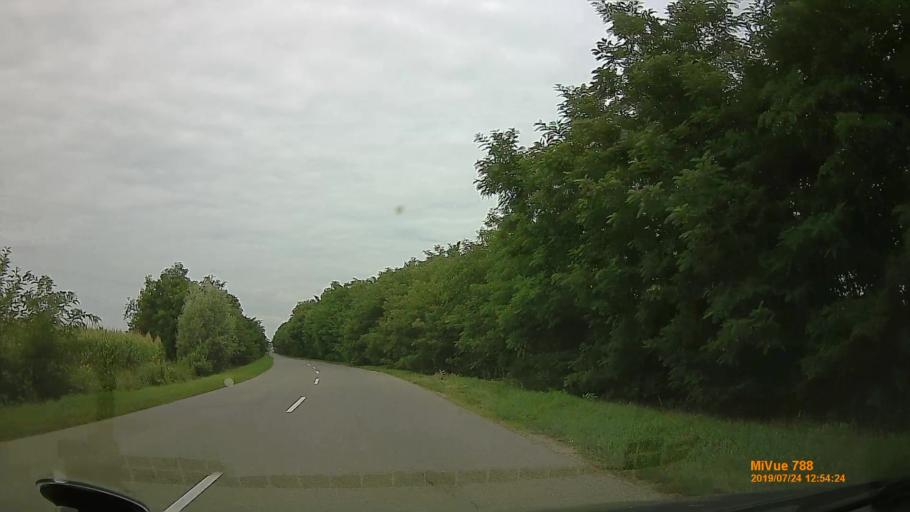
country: HU
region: Szabolcs-Szatmar-Bereg
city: Aranyosapati
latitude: 48.2151
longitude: 22.2993
